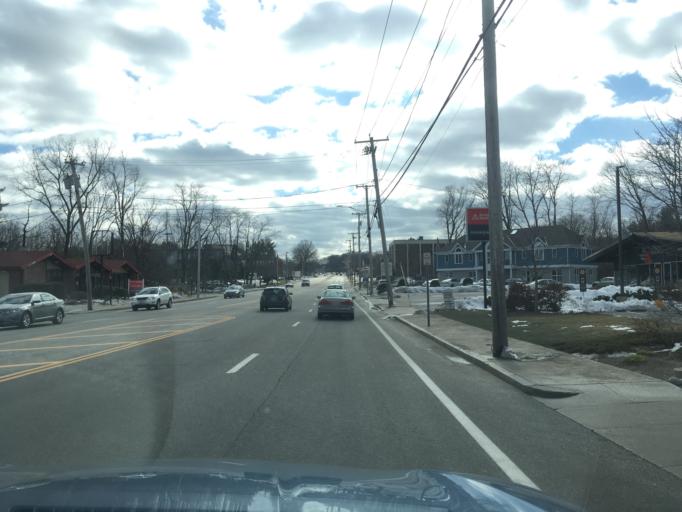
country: US
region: Rhode Island
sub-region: Providence County
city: Cranston
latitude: 41.7717
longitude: -71.4530
